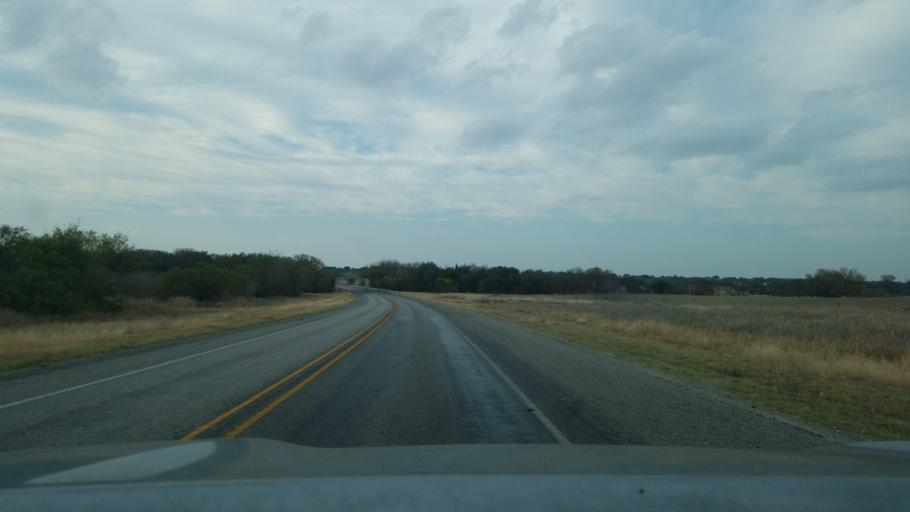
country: US
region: Texas
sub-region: Mills County
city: Goldthwaite
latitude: 31.5114
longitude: -98.5840
